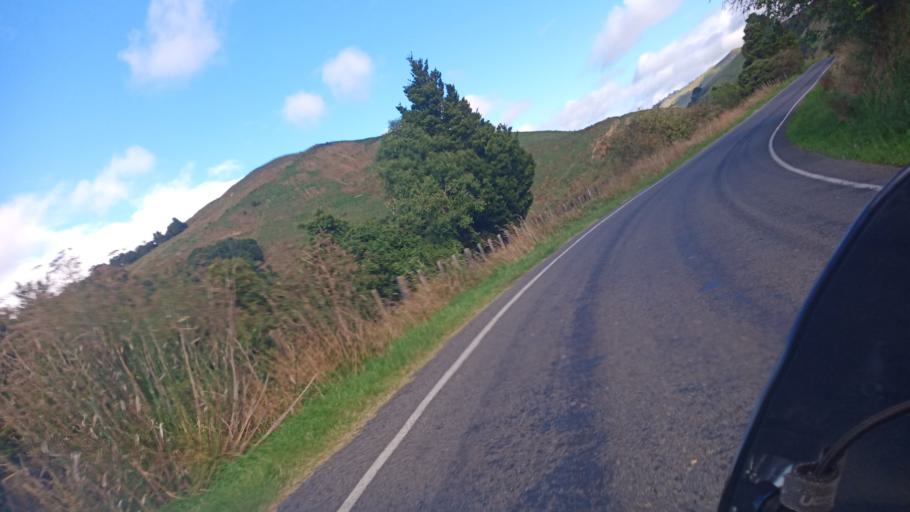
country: NZ
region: Gisborne
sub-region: Gisborne District
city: Gisborne
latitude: -38.5323
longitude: 177.5512
